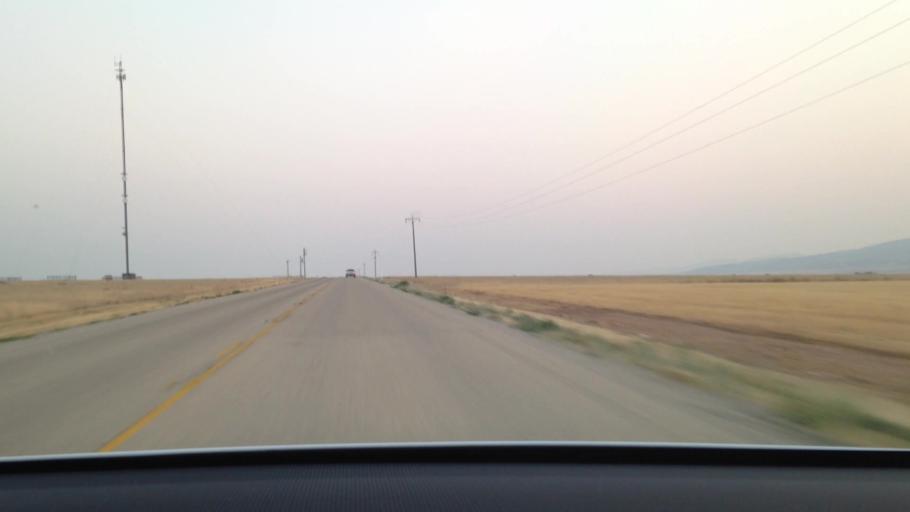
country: US
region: Utah
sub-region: Juab County
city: Nephi
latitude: 39.6541
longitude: -111.8573
